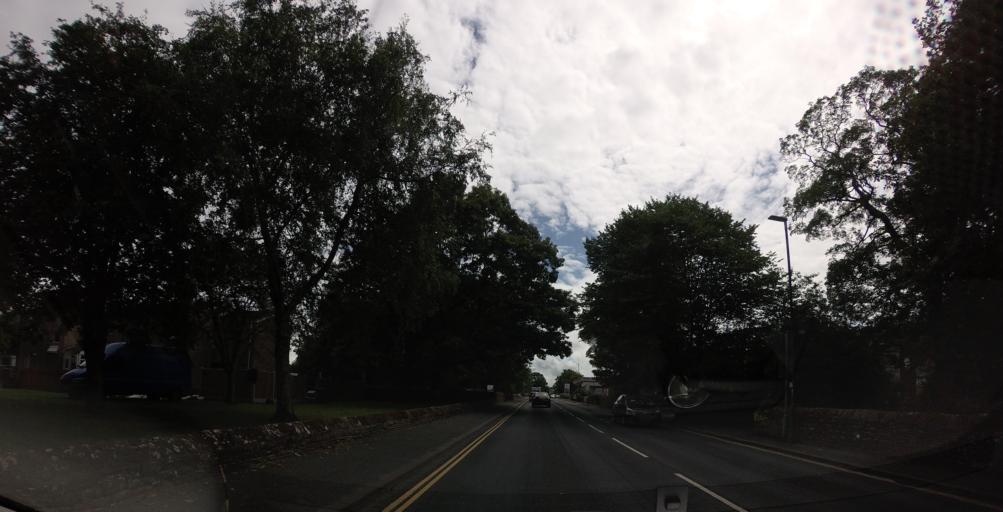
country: GB
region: England
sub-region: Cumbria
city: Penrith
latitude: 54.6585
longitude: -2.7462
